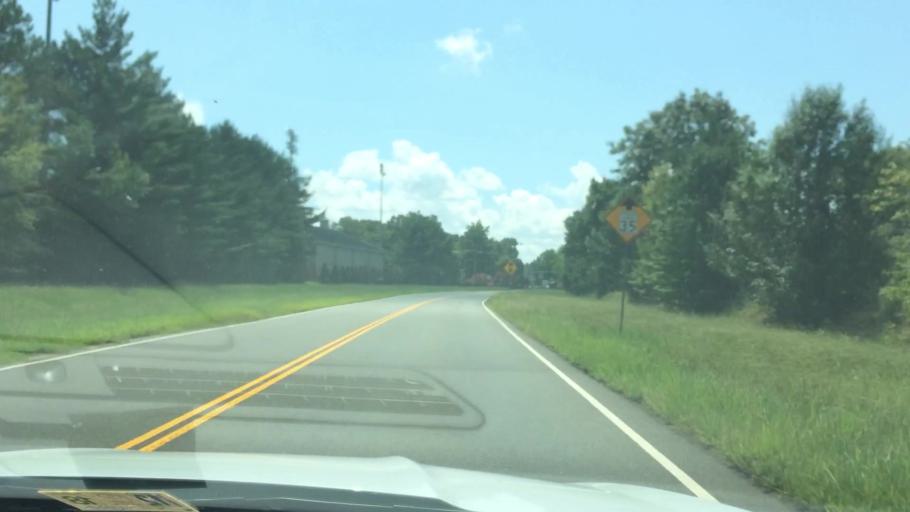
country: US
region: Virginia
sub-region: James City County
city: Williamsburg
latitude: 37.2919
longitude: -76.7341
